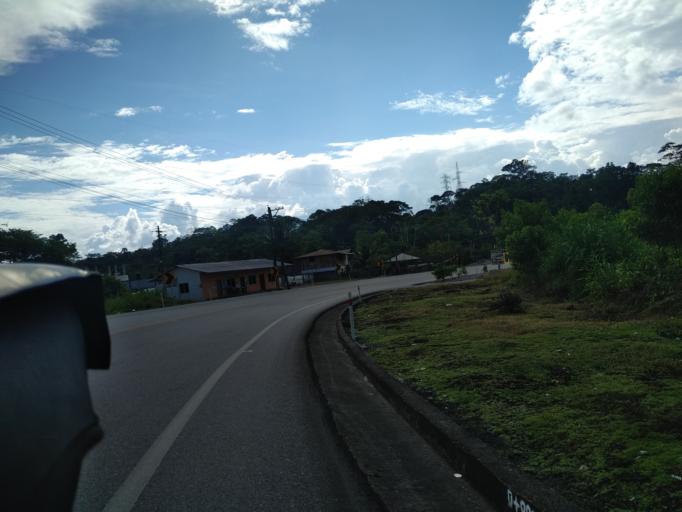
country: EC
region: Napo
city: Tena
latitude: -1.0481
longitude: -77.7956
